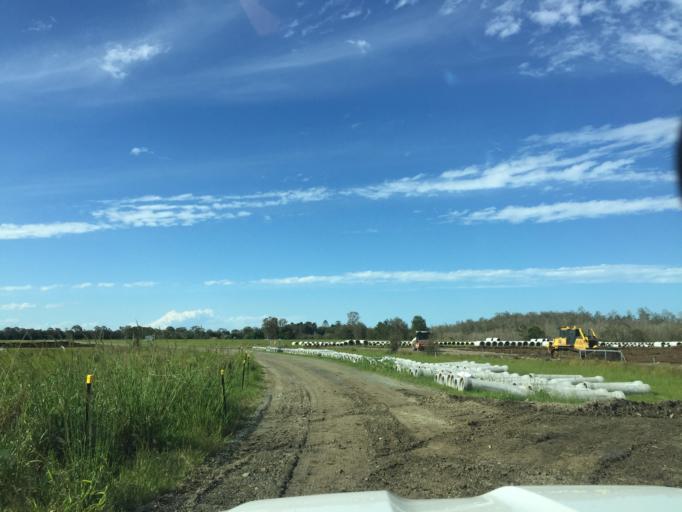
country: AU
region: Queensland
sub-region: Moreton Bay
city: Morayfield
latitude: -27.1157
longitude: 152.9942
